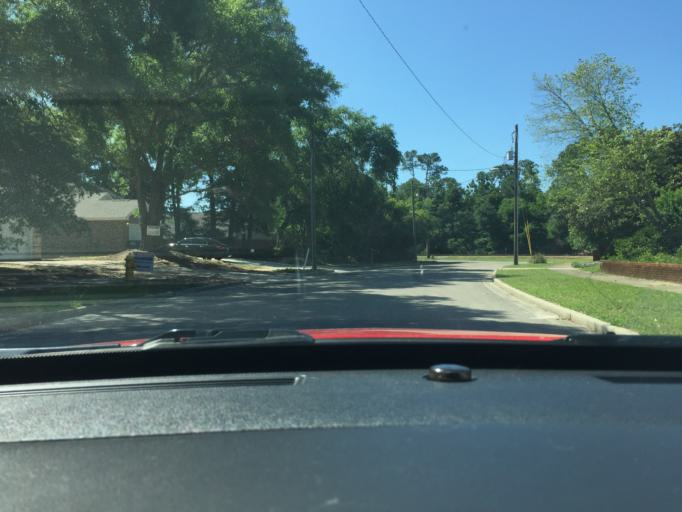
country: US
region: Mississippi
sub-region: Harrison County
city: D'Iberville
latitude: 30.3948
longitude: -88.9898
